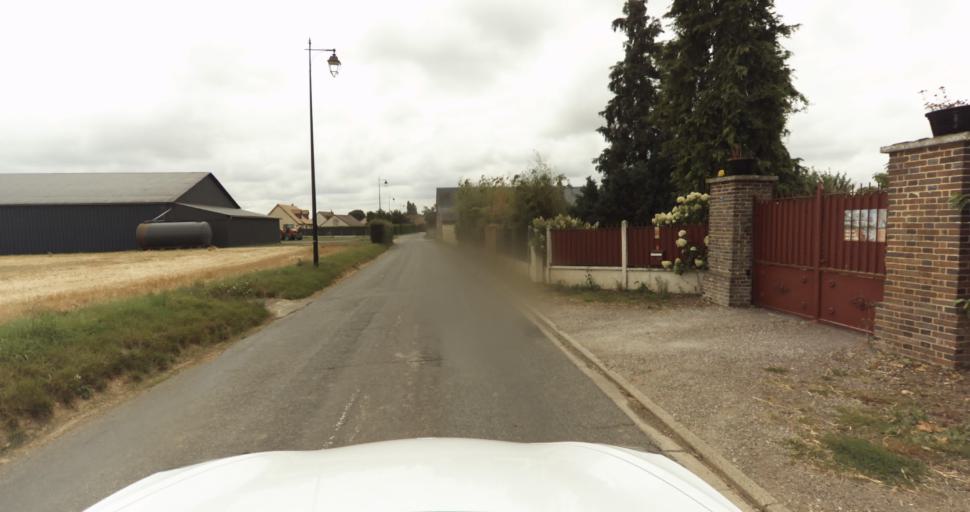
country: FR
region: Haute-Normandie
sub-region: Departement de l'Eure
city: Claville
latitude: 49.0307
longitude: 1.0306
